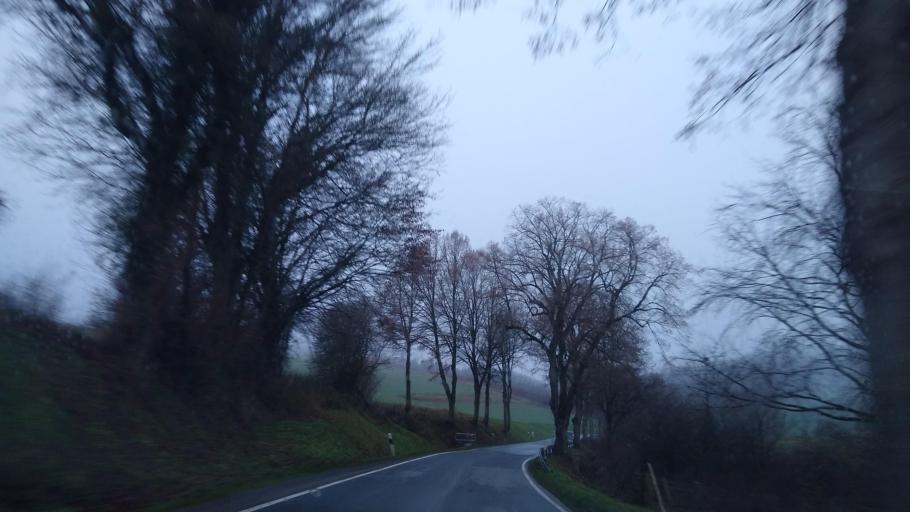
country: DE
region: Lower Saxony
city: Ottenstein
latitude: 51.9410
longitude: 9.3930
